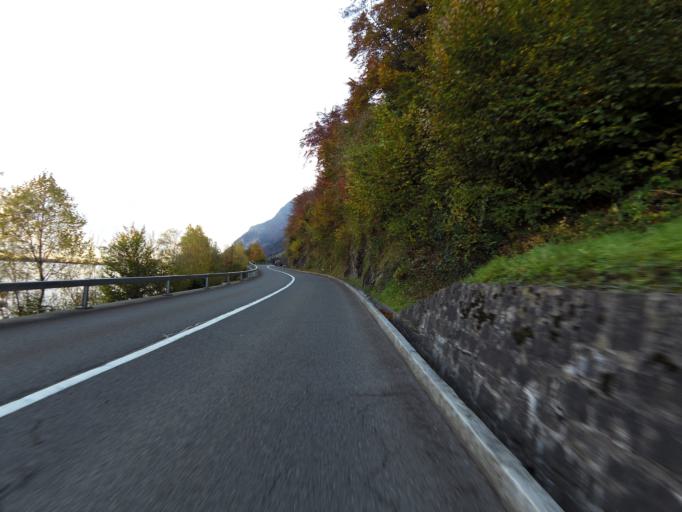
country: CH
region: Uri
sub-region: Uri
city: Flueelen
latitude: 46.9031
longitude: 8.5923
